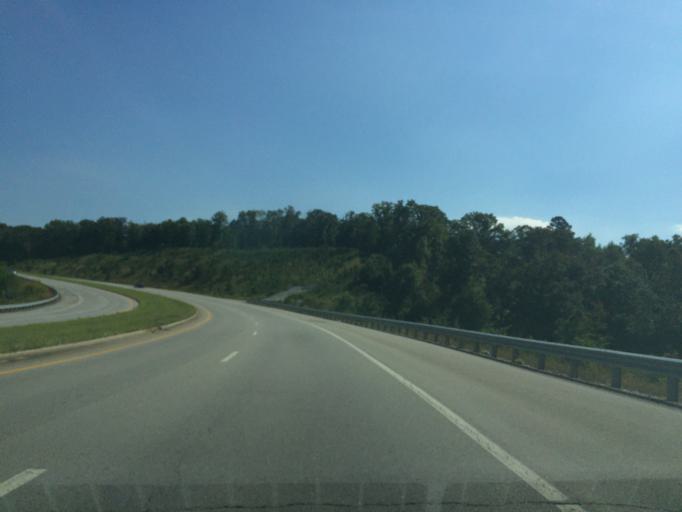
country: US
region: Tennessee
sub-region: Hamilton County
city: Harrison
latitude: 35.0727
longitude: -85.1237
